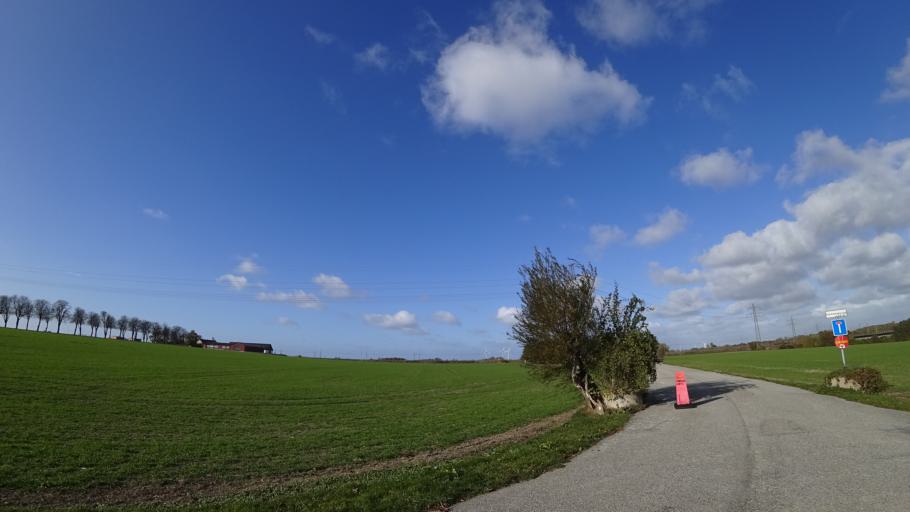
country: SE
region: Skane
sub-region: Staffanstorps Kommun
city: Hjaerup
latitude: 55.6870
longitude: 13.1659
